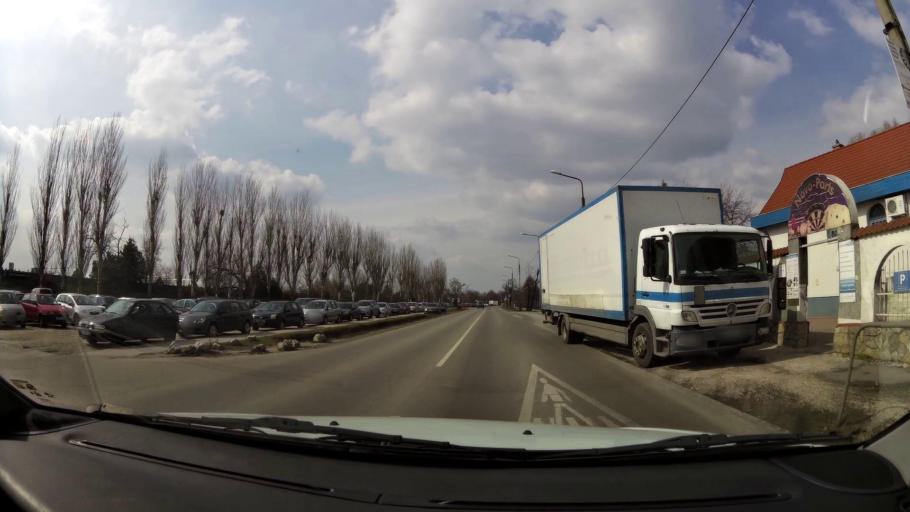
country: HU
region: Budapest
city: Budapest XVI. keruelet
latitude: 47.5295
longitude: 19.1497
